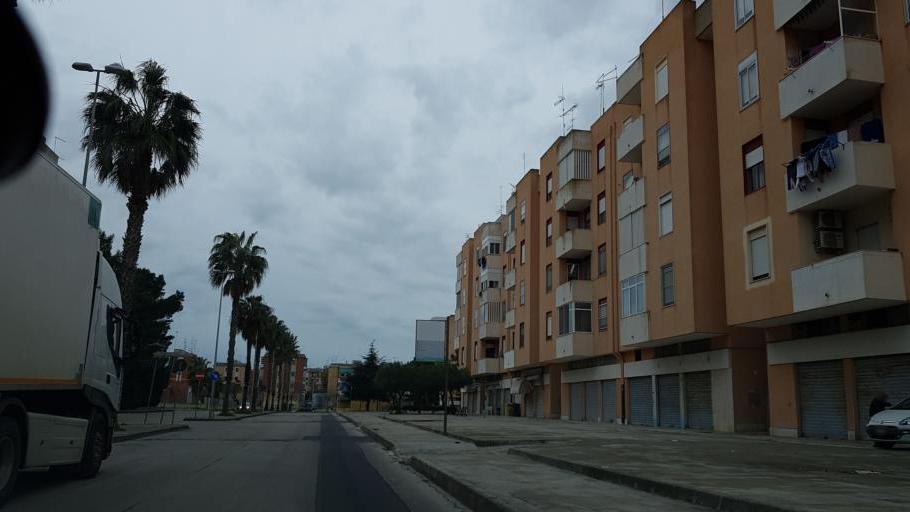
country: IT
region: Apulia
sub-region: Provincia di Brindisi
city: Brindisi
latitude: 40.6196
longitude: 17.9283
